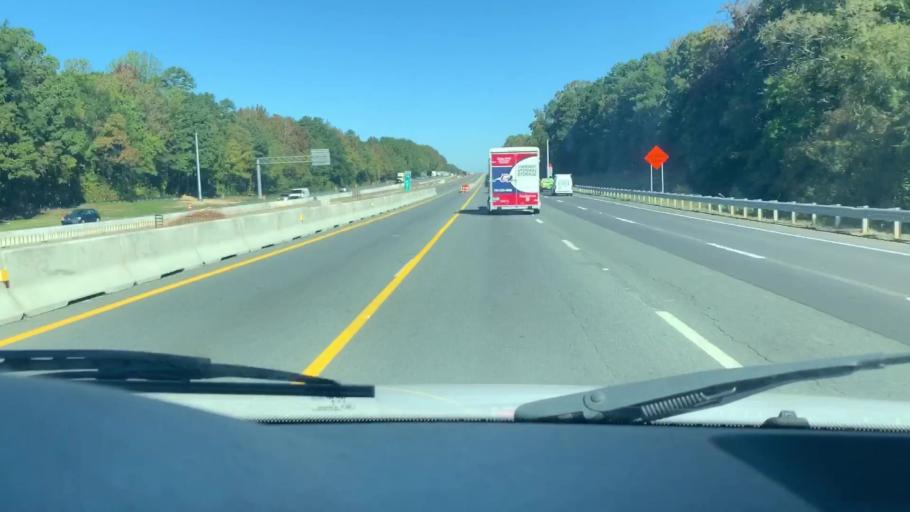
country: US
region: North Carolina
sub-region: Mecklenburg County
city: Charlotte
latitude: 35.3159
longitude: -80.8473
